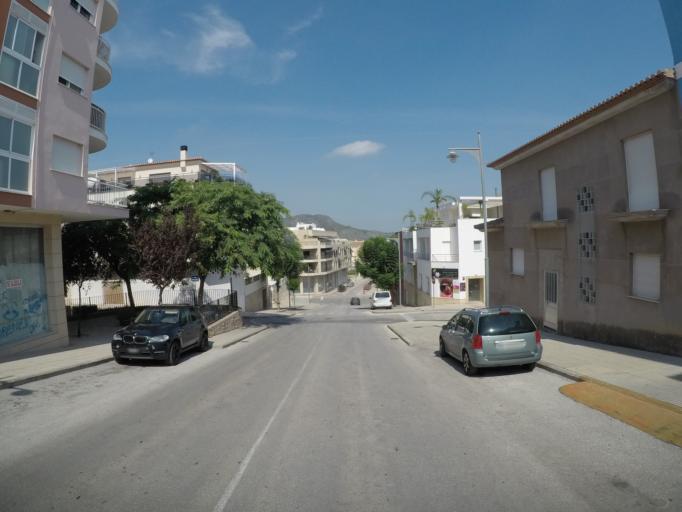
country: ES
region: Valencia
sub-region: Provincia de Alicante
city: Pego
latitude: 38.8423
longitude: -0.1131
